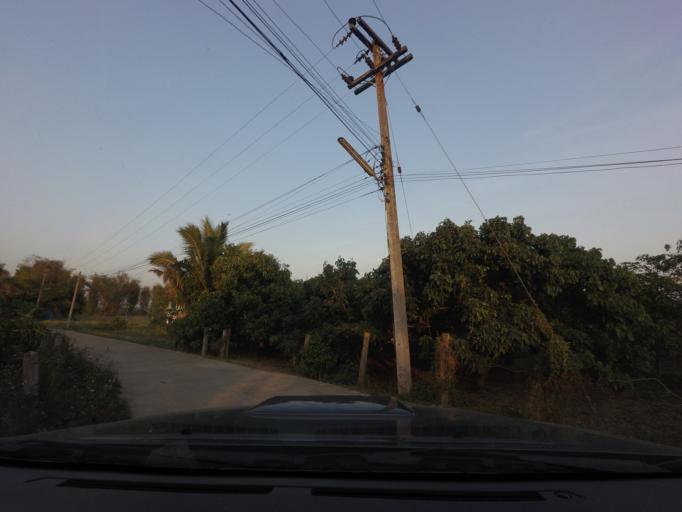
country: TH
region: Chiang Mai
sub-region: Amphoe Chiang Dao
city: Chiang Dao
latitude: 19.3679
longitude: 98.9579
